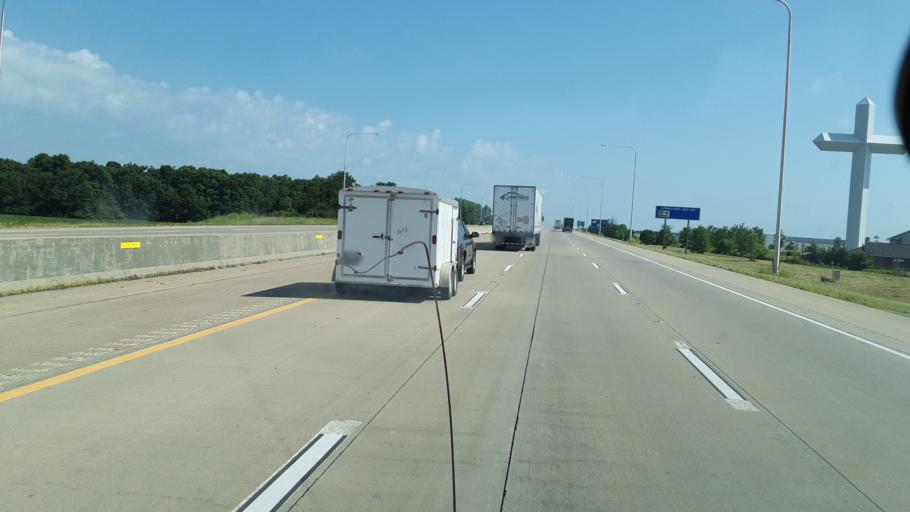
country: US
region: Illinois
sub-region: Effingham County
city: Effingham
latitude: 39.1052
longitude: -88.5733
